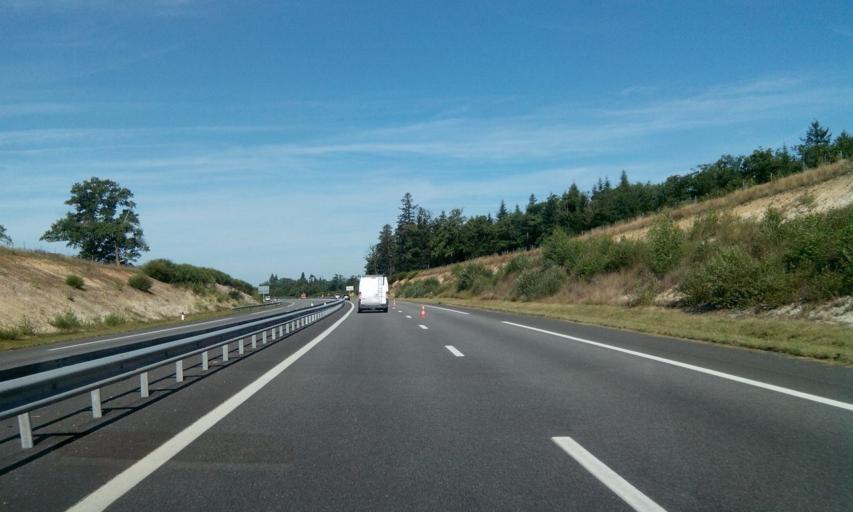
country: FR
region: Limousin
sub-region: Departement de la Haute-Vienne
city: Veyrac
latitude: 45.8865
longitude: 1.0760
